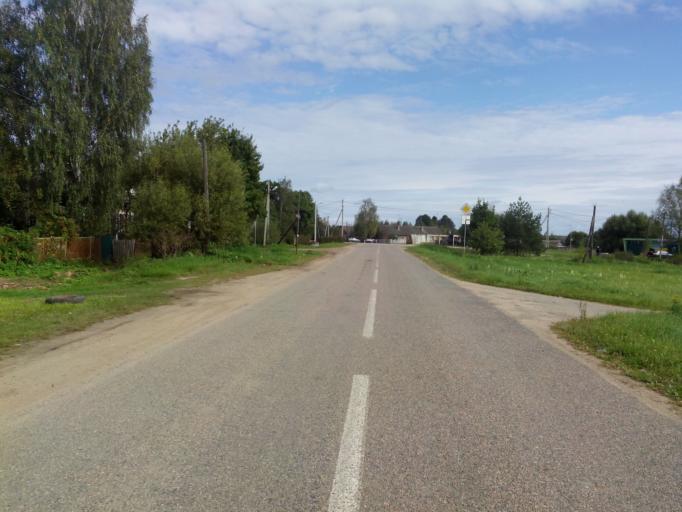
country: RU
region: Moskovskaya
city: Severnyy
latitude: 56.6461
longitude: 37.7293
